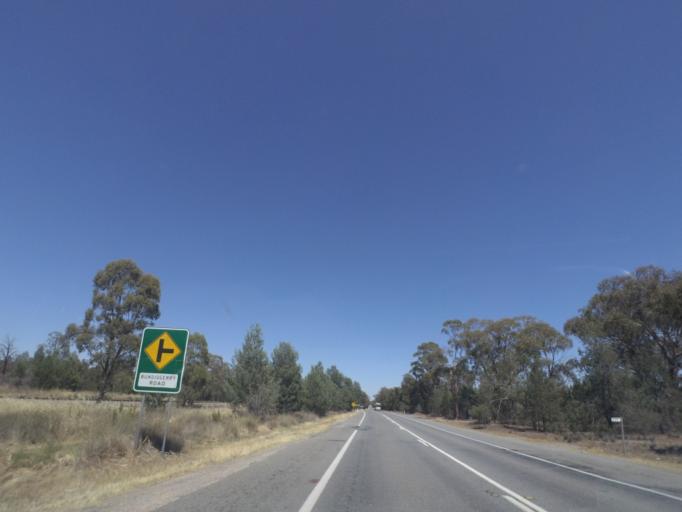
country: AU
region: New South Wales
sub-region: Narrandera
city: Narrandera
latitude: -34.7363
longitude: 146.5983
